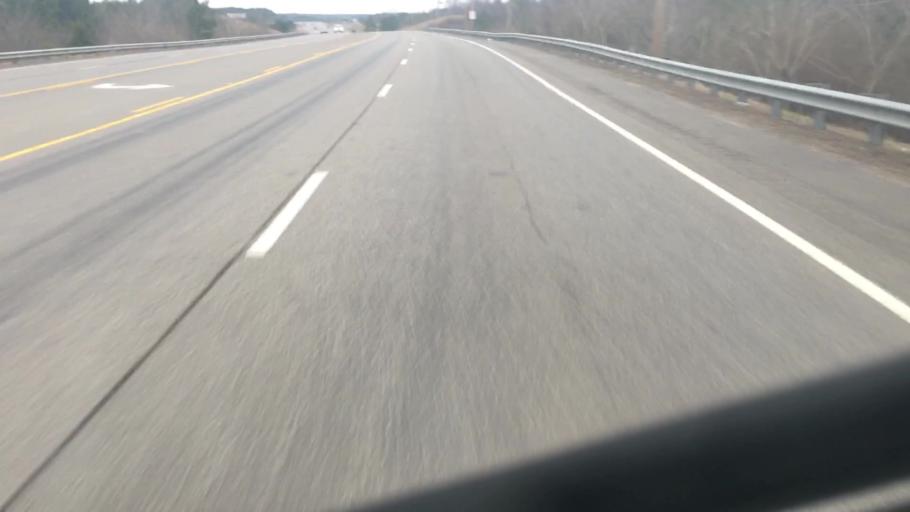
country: US
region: Alabama
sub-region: Walker County
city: Jasper
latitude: 33.8008
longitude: -87.2363
